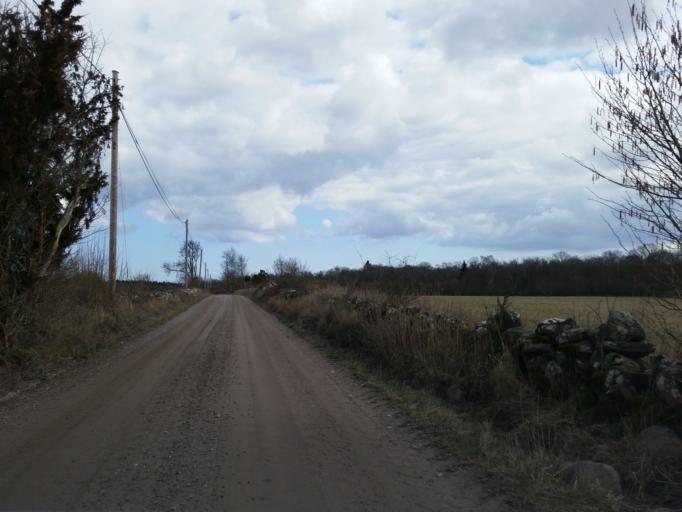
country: SE
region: Kalmar
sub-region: Morbylanga Kommun
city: Sodra Sandby
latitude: 56.6776
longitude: 16.6054
